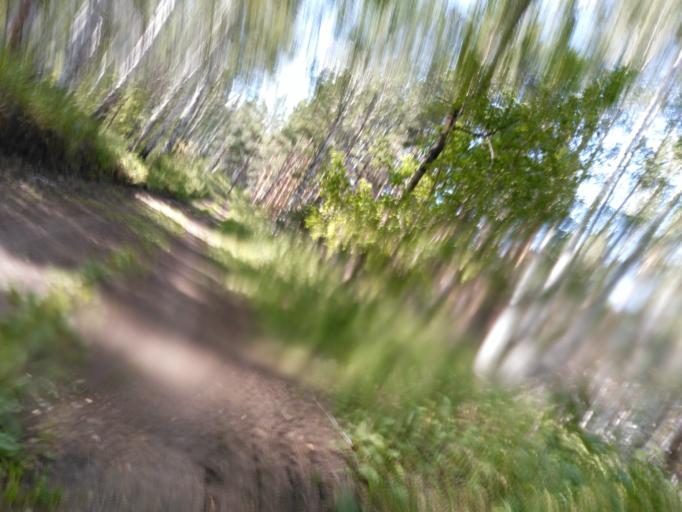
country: RU
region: Bashkortostan
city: Uchaly
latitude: 54.3289
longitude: 59.3596
